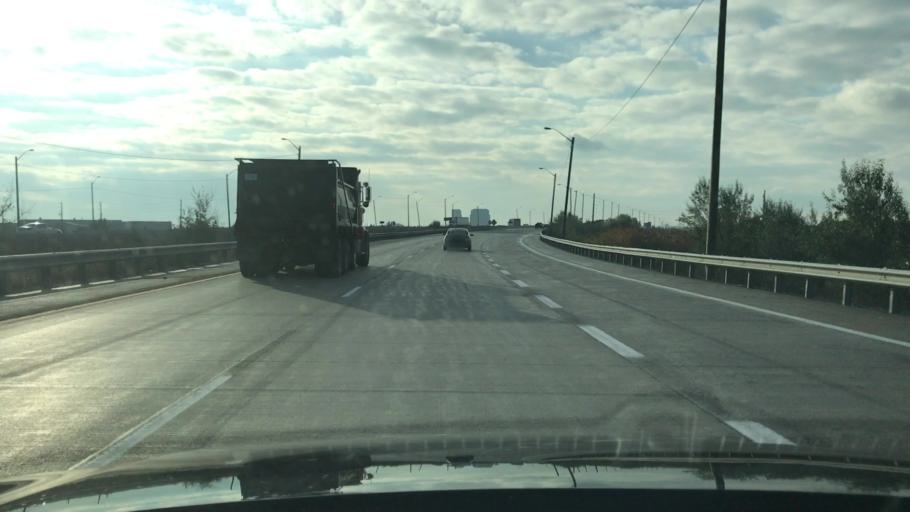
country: CA
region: Ontario
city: Etobicoke
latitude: 43.7497
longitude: -79.6315
